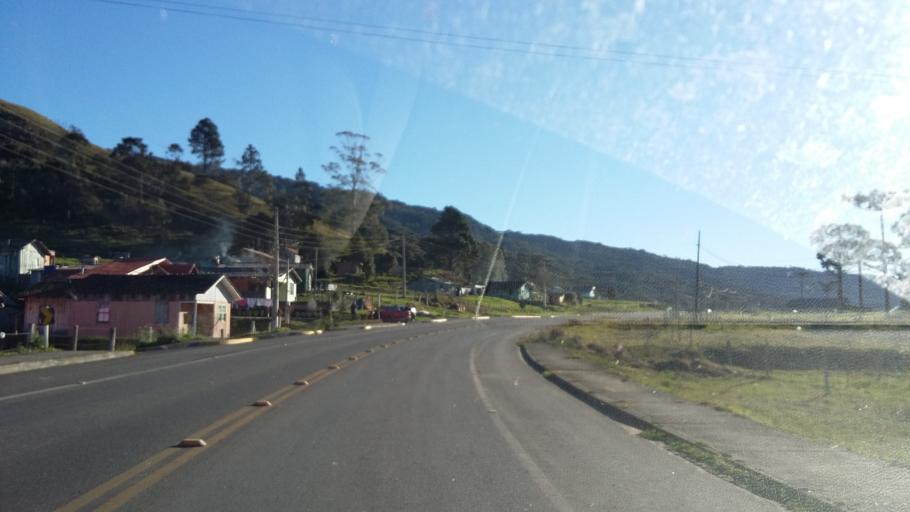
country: BR
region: Santa Catarina
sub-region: Lauro Muller
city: Lauro Muller
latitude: -28.0194
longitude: -49.5125
